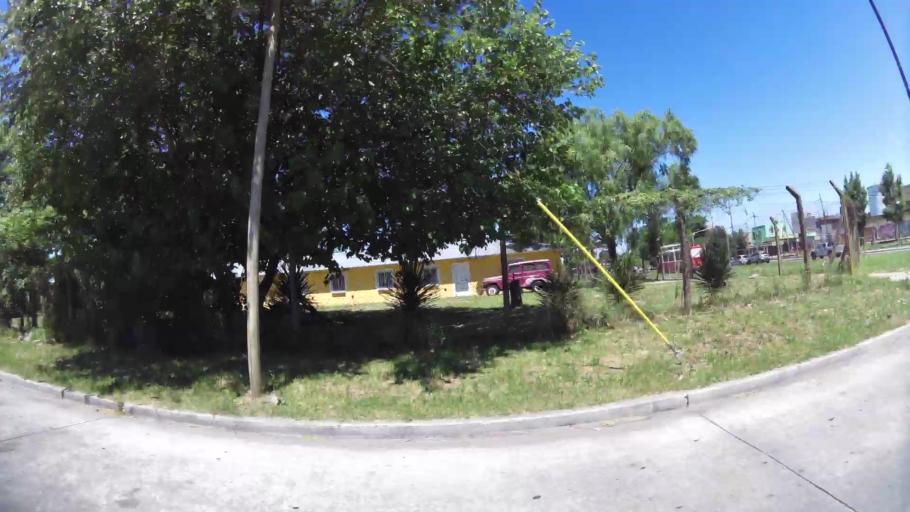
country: AR
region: Buenos Aires
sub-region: Partido de Tigre
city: Tigre
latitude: -34.4906
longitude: -58.5887
